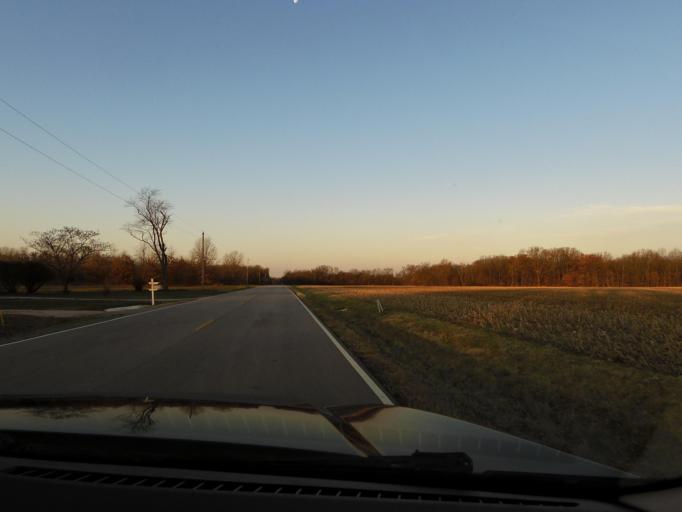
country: US
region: Illinois
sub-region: Marion County
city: Salem
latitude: 38.7585
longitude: -88.9338
